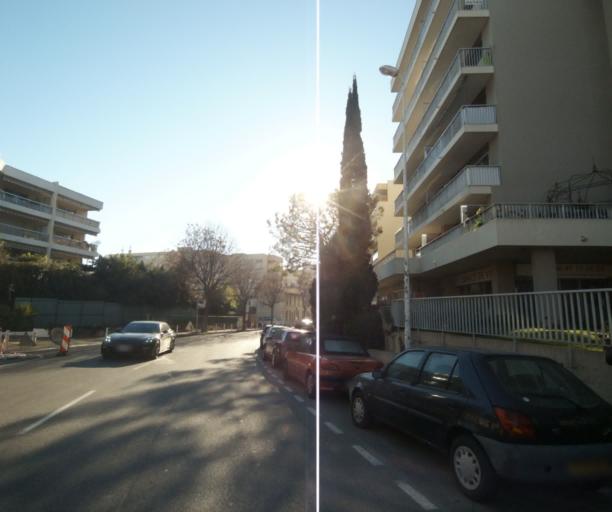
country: FR
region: Provence-Alpes-Cote d'Azur
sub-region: Departement des Alpes-Maritimes
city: Antibes
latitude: 43.5846
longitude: 7.1146
